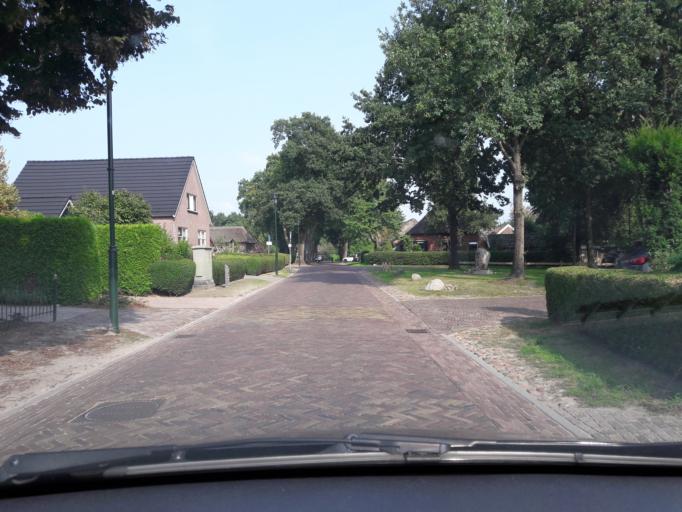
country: NL
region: Drenthe
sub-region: Gemeente Borger-Odoorn
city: Borger
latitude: 52.9284
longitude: 6.7920
